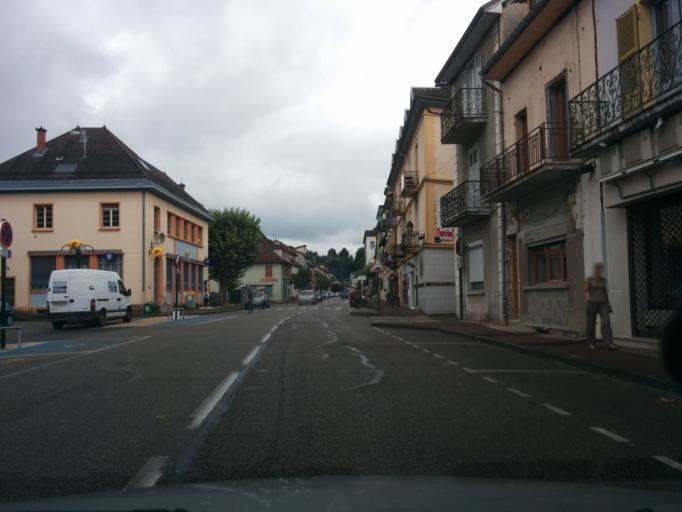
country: FR
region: Rhone-Alpes
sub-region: Departement de la Savoie
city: Le Pont-de-Beauvoisin
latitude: 45.5349
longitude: 5.6710
